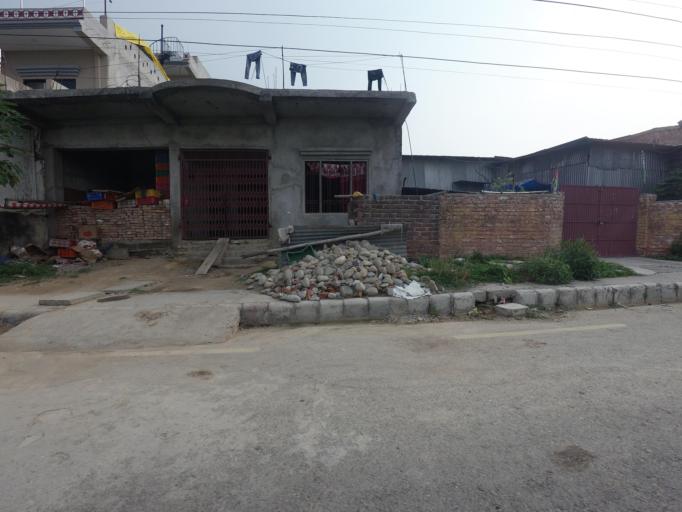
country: NP
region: Western Region
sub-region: Lumbini Zone
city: Bhairahawa
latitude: 27.5050
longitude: 83.4451
